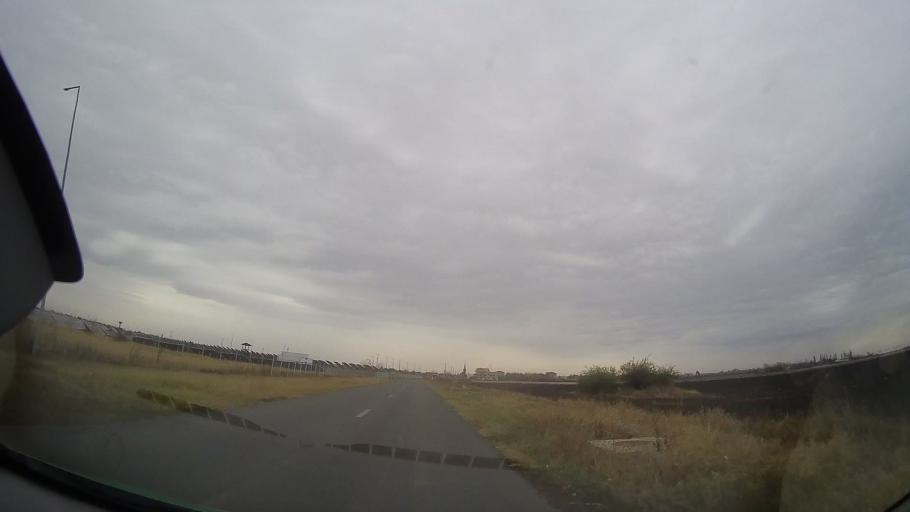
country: RO
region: Prahova
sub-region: Oras Mizil
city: Mizil
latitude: 45.0069
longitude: 26.4239
